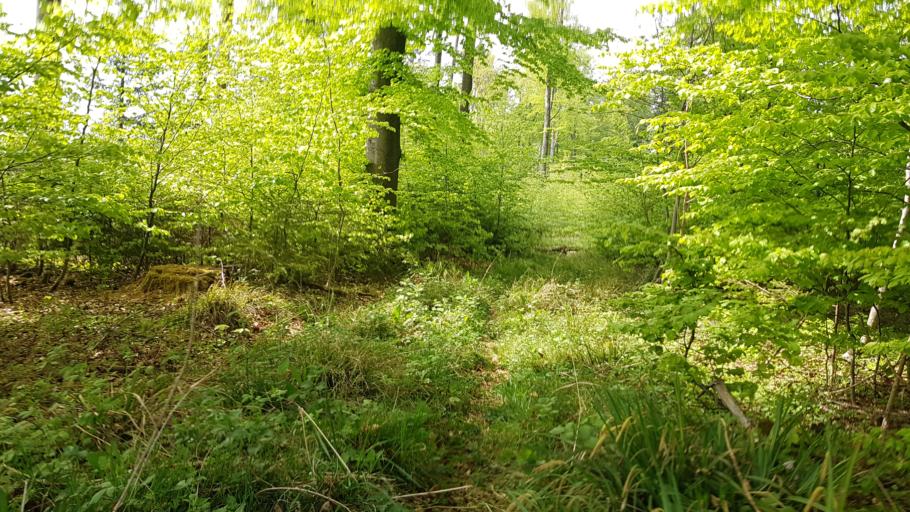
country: CH
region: Aargau
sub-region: Bezirk Kulm
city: Reinach
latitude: 47.2863
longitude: 8.1748
